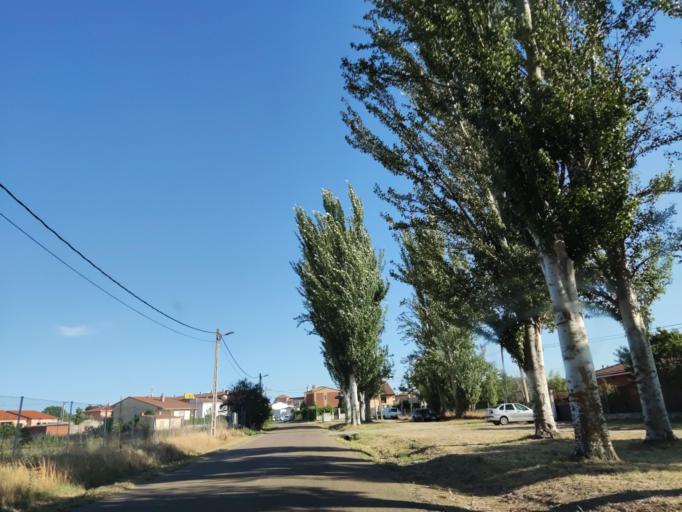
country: ES
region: Castille and Leon
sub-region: Provincia de Zamora
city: Villaralbo
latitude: 41.4962
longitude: -5.6846
